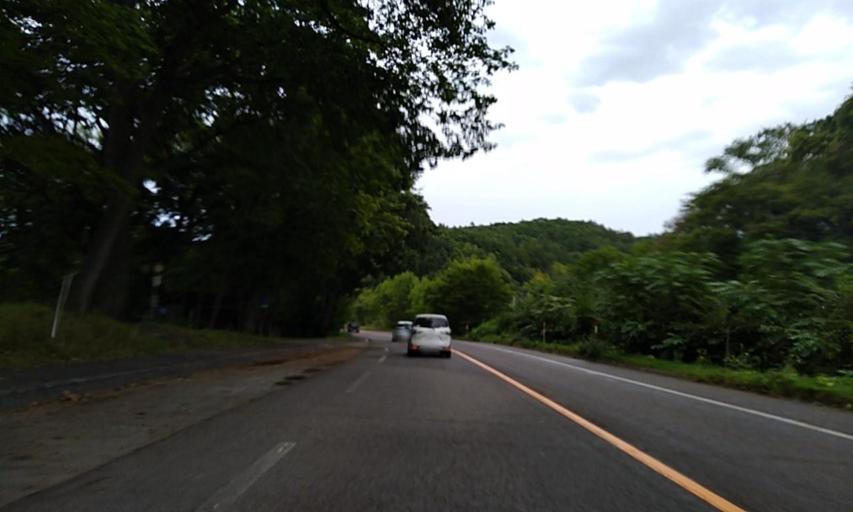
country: JP
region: Hokkaido
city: Abashiri
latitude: 43.9831
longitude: 144.2196
